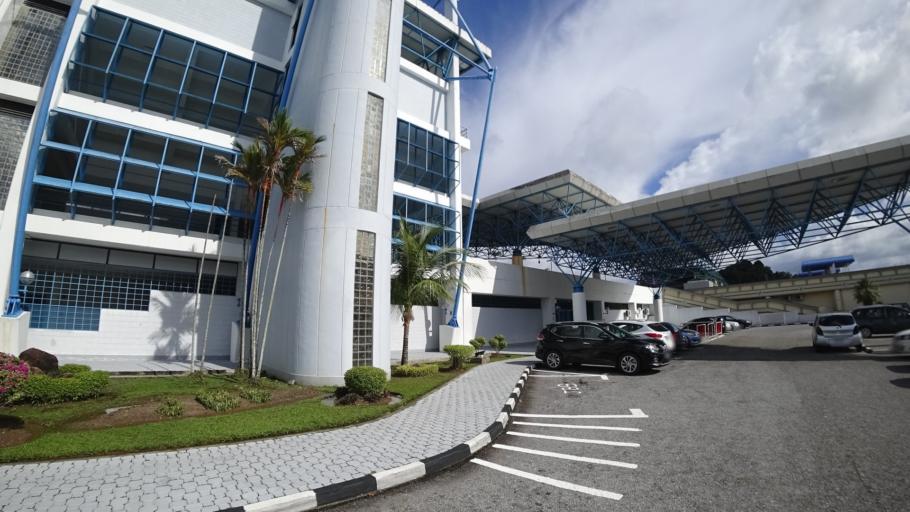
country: BN
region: Brunei and Muara
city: Bandar Seri Begawan
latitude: 4.9297
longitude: 114.9467
